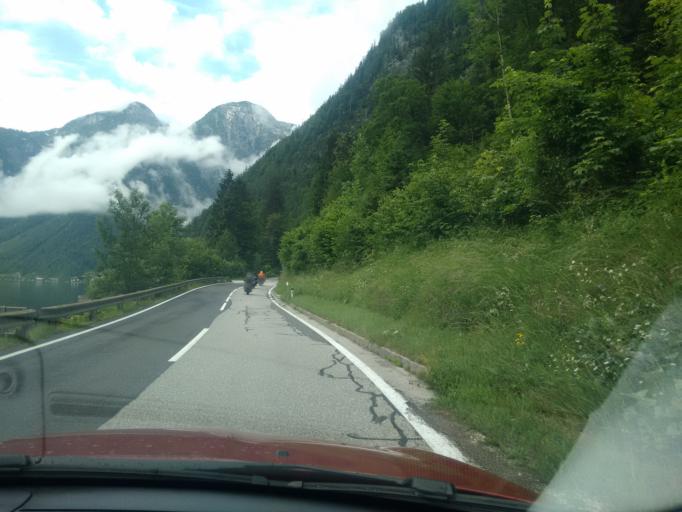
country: AT
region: Upper Austria
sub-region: Politischer Bezirk Gmunden
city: Bad Goisern
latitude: 47.5742
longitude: 13.6518
